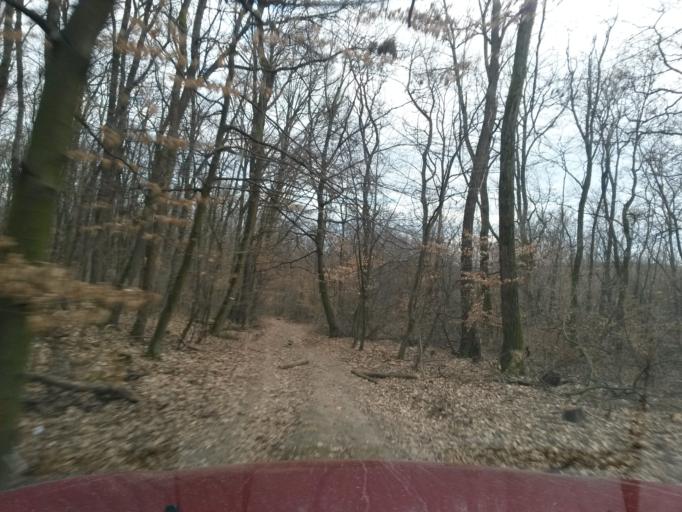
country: SK
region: Kosicky
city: Kosice
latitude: 48.6966
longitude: 21.2983
